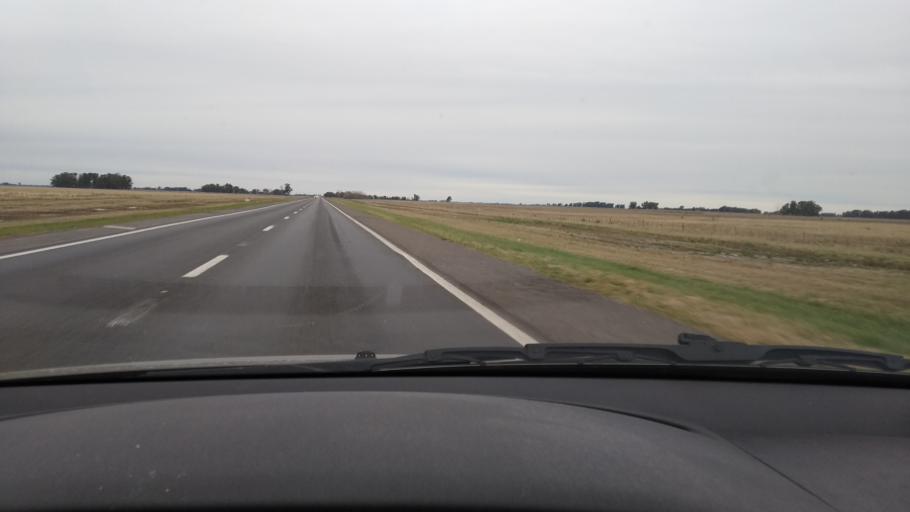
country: AR
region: Buenos Aires
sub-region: Partido de Las Flores
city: Las Flores
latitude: -36.1565
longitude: -59.2173
